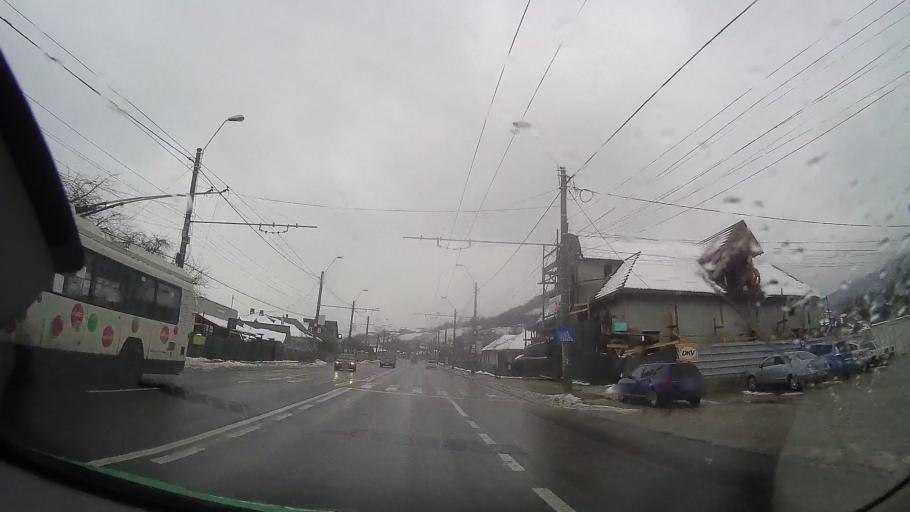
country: RO
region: Neamt
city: Piatra Neamt
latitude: 46.9401
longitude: 26.3313
